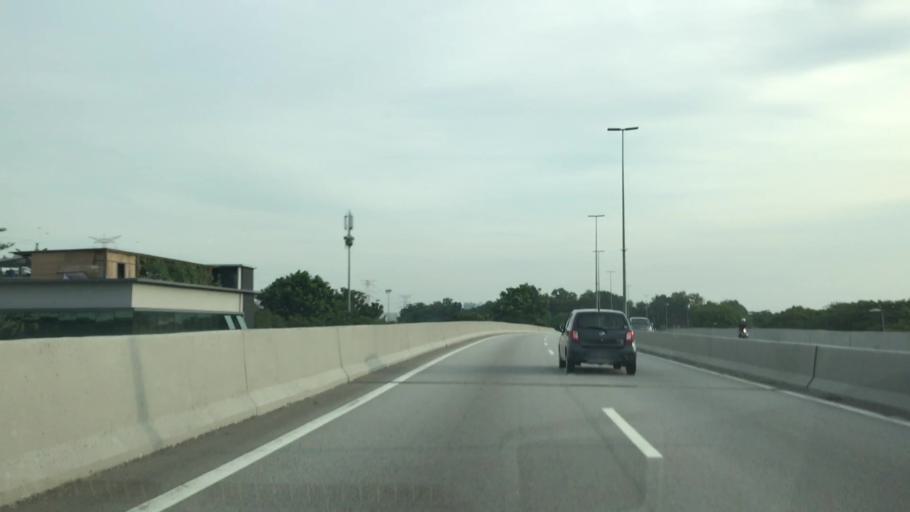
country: MY
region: Kuala Lumpur
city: Kuala Lumpur
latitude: 3.1126
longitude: 101.7124
